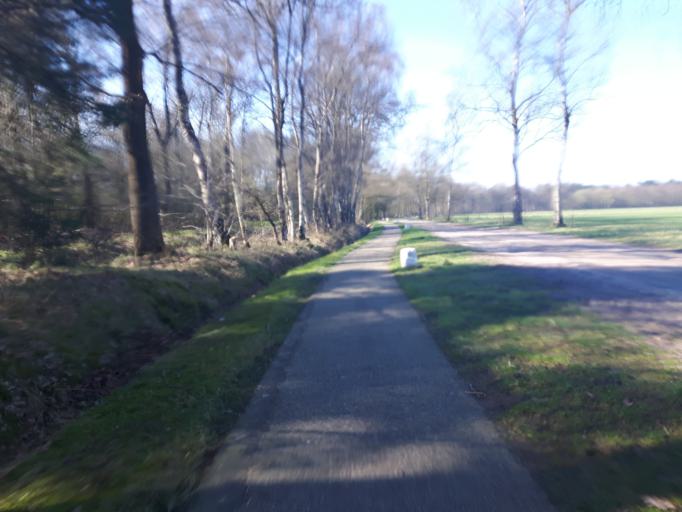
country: NL
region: Overijssel
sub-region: Gemeente Enschede
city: Enschede
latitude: 52.1822
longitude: 6.8294
